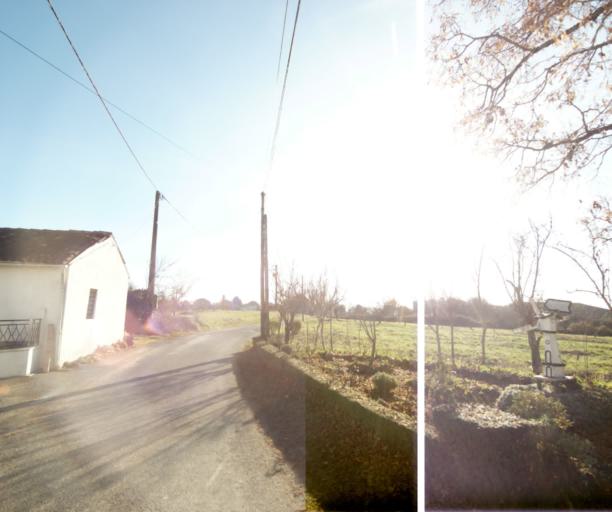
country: FR
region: Poitou-Charentes
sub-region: Departement de la Charente-Maritime
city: Cherac
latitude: 45.7057
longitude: -0.4507
